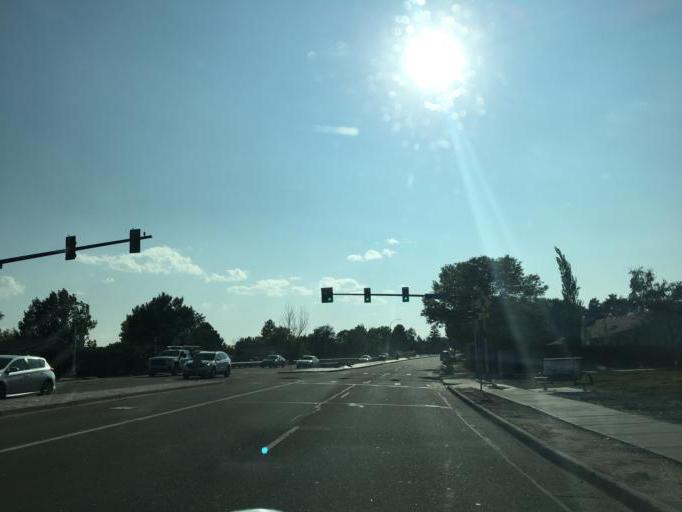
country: US
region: Colorado
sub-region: Adams County
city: Westminster
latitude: 39.8415
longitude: -105.0618
